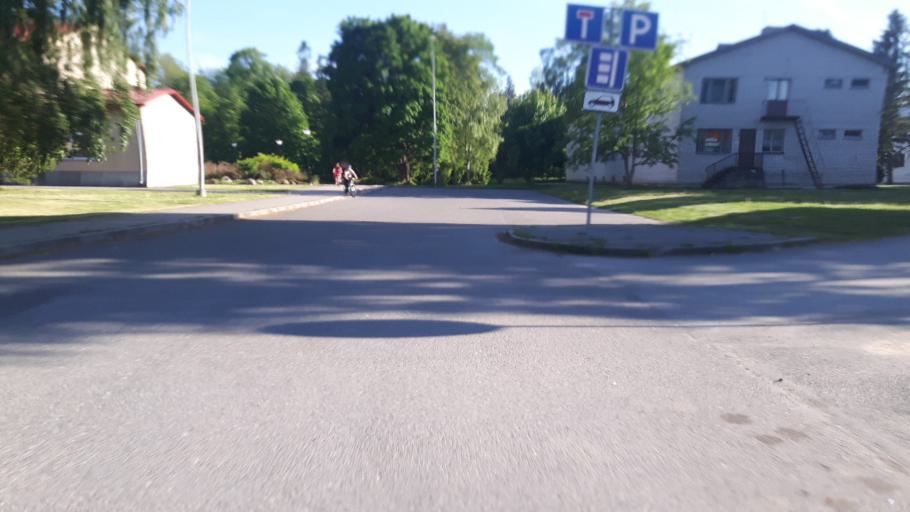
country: EE
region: Raplamaa
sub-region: Kehtna vald
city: Kehtna
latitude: 58.9256
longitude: 24.8720
